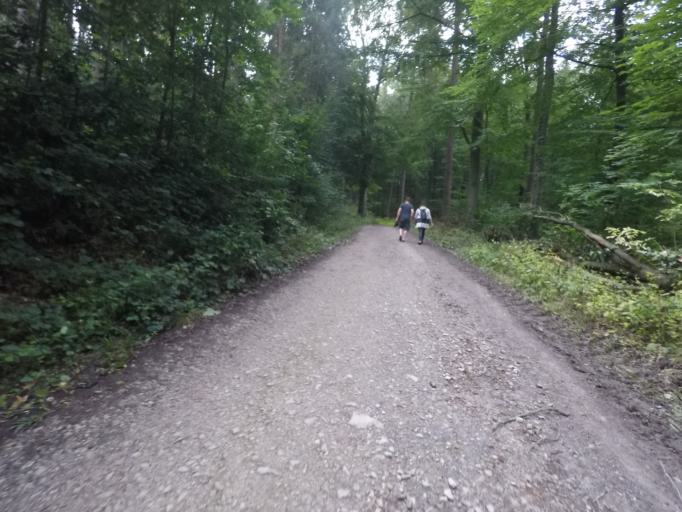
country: DE
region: North Rhine-Westphalia
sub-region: Regierungsbezirk Detmold
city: Bielefeld
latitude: 52.0312
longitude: 8.4941
